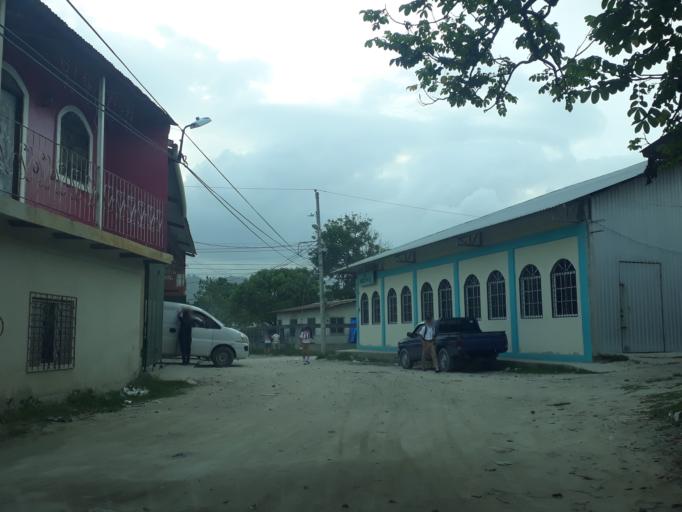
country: HN
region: Cortes
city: Choloma
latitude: 15.5731
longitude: -87.9494
